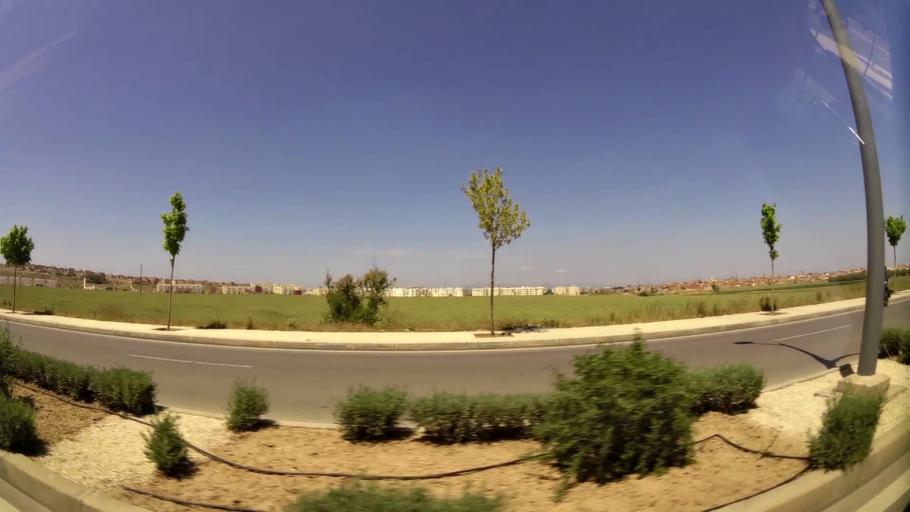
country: MA
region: Oriental
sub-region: Oujda-Angad
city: Oujda
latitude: 34.6956
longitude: -1.9327
